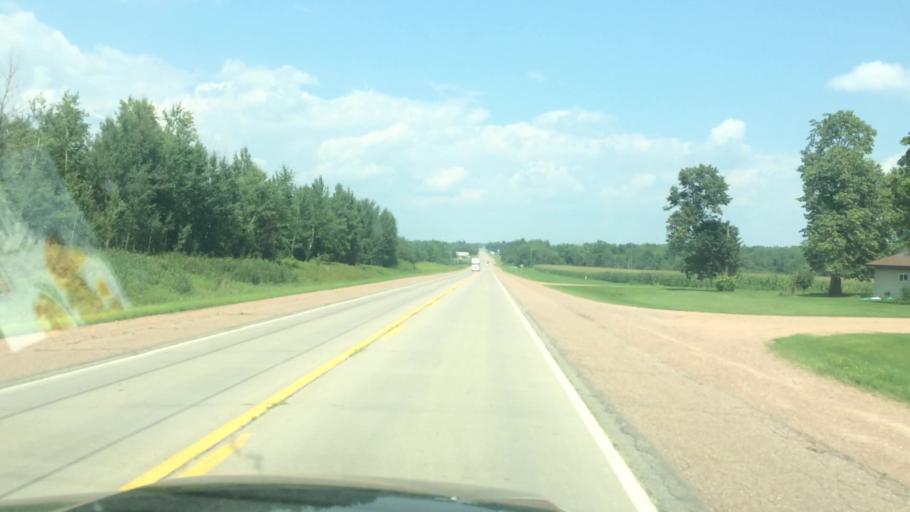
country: US
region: Wisconsin
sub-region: Clark County
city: Colby
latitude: 44.8834
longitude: -90.3155
